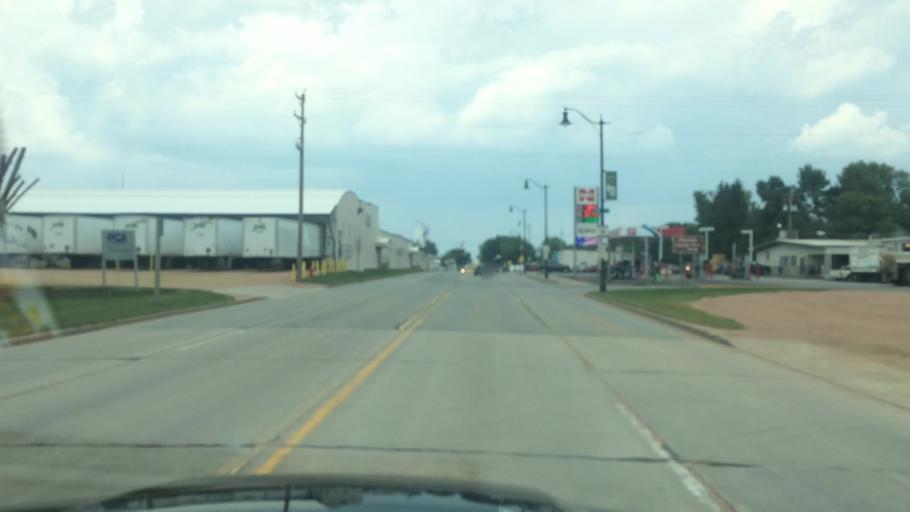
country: US
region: Wisconsin
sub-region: Clark County
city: Colby
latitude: 44.9019
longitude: -90.3150
